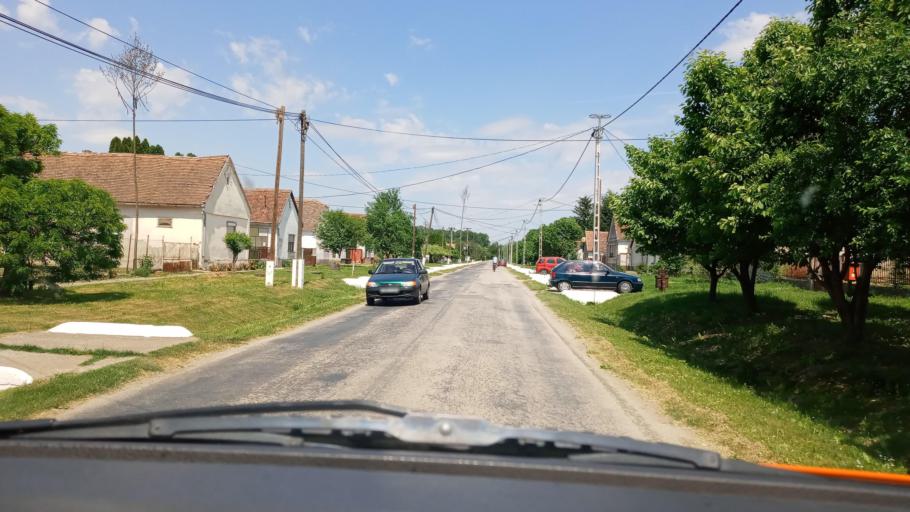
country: HR
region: Osjecko-Baranjska
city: Viljevo
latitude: 45.8128
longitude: 18.1177
